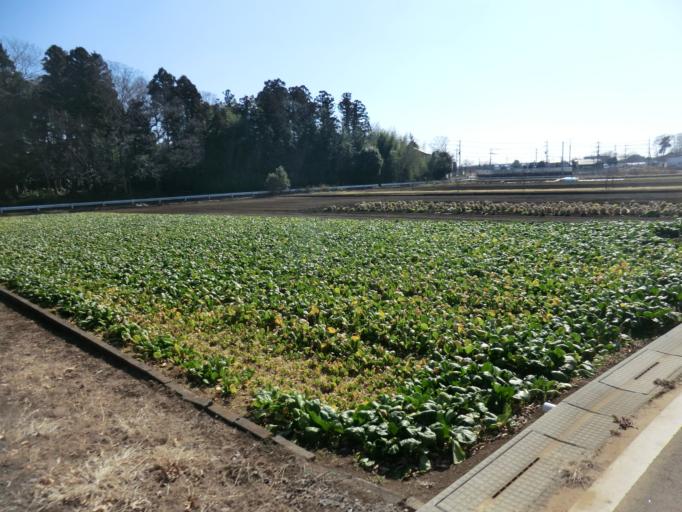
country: JP
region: Ibaraki
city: Naka
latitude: 36.0465
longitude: 140.1169
